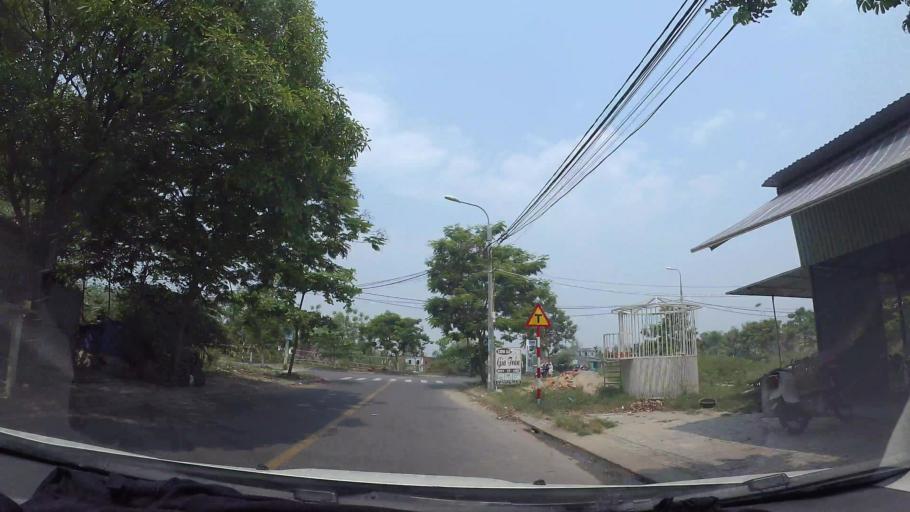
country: VN
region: Da Nang
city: Cam Le
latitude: 16.0082
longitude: 108.2139
